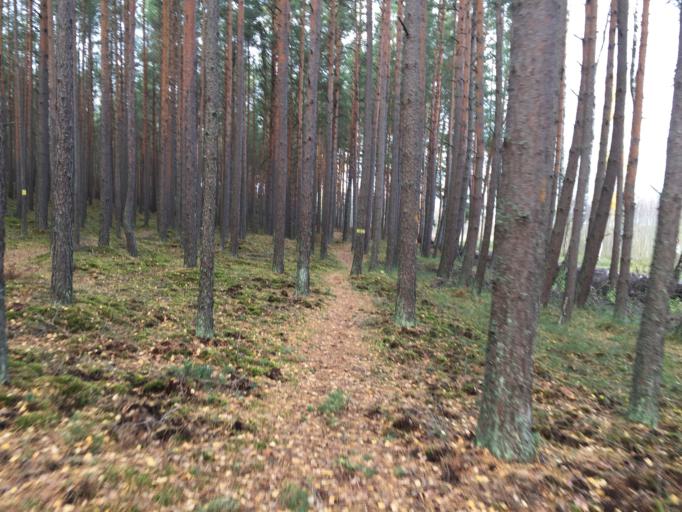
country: LV
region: Carnikava
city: Carnikava
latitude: 57.1475
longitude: 24.2633
